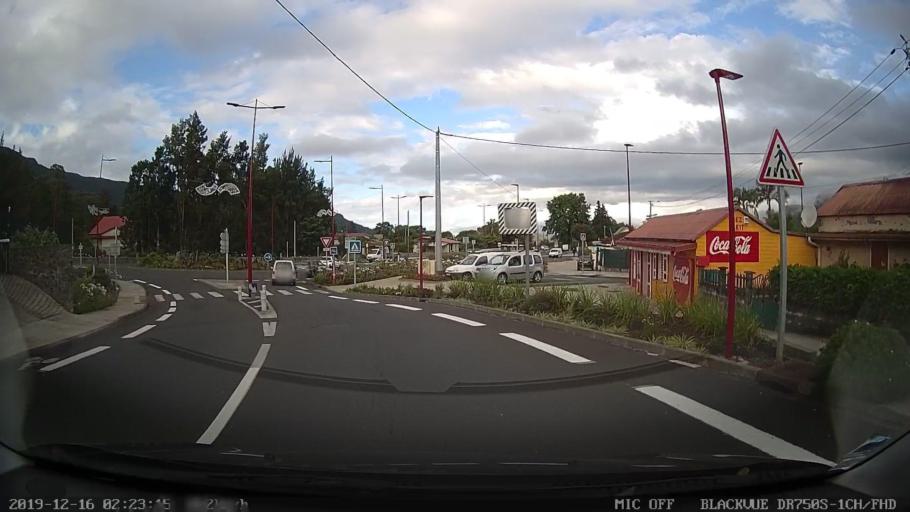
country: RE
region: Reunion
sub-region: Reunion
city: Salazie
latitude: -21.1436
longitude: 55.6202
